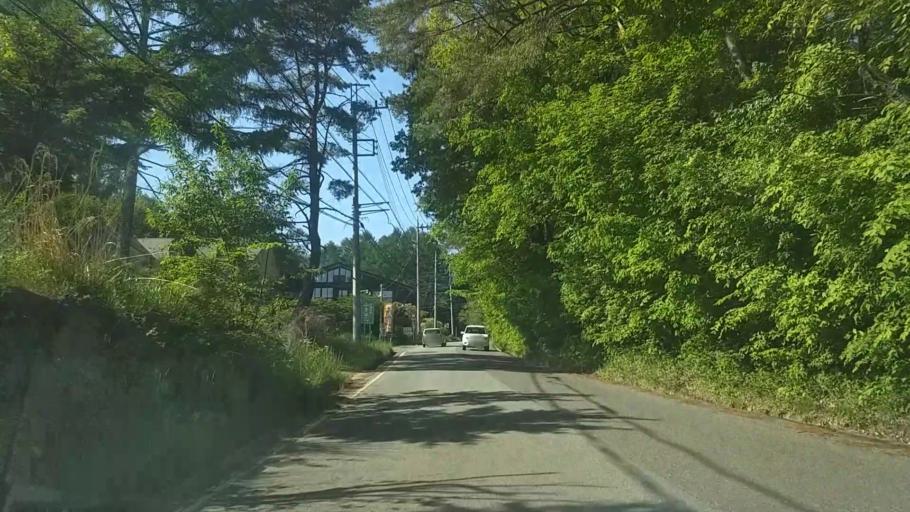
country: JP
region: Yamanashi
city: Nirasaki
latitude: 35.8798
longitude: 138.3565
